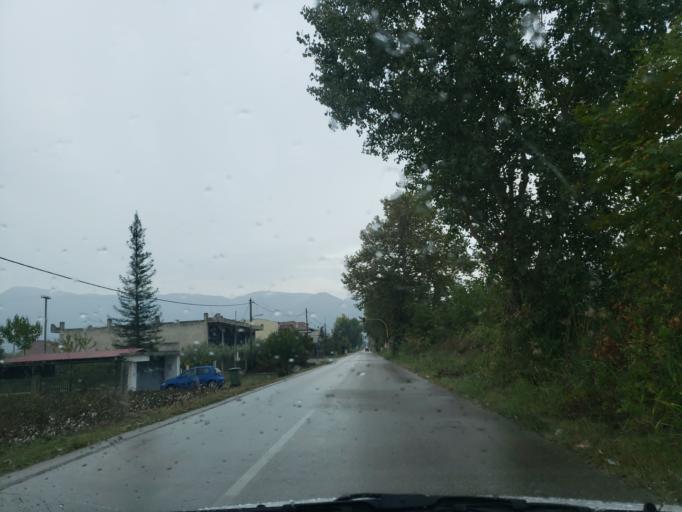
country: GR
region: Central Greece
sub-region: Nomos Fthiotidos
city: Anthili
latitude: 38.8291
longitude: 22.4415
